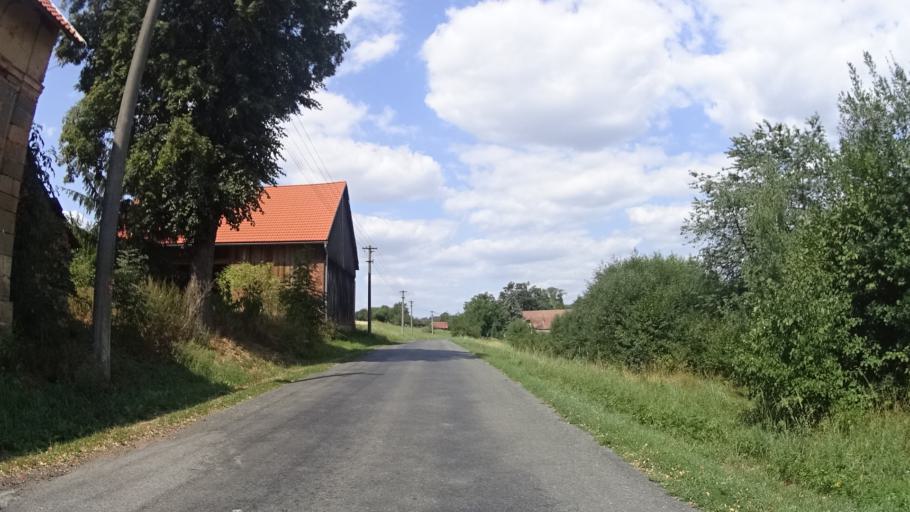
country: CZ
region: Kralovehradecky
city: Kopidlno
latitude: 50.3948
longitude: 15.2859
